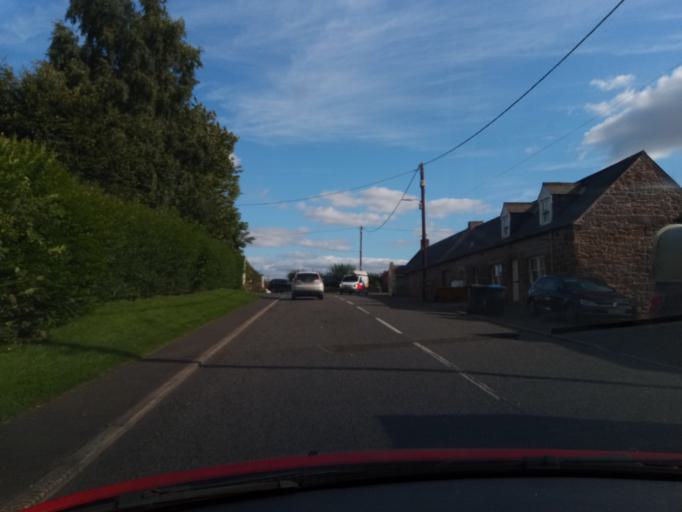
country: GB
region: Scotland
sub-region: The Scottish Borders
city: Coldstream
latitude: 55.7190
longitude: -2.2678
